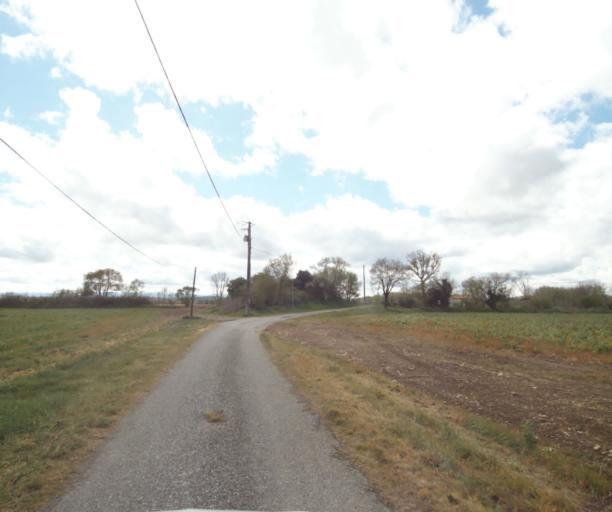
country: FR
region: Midi-Pyrenees
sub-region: Departement de l'Ariege
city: Saverdun
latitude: 43.2660
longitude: 1.5885
